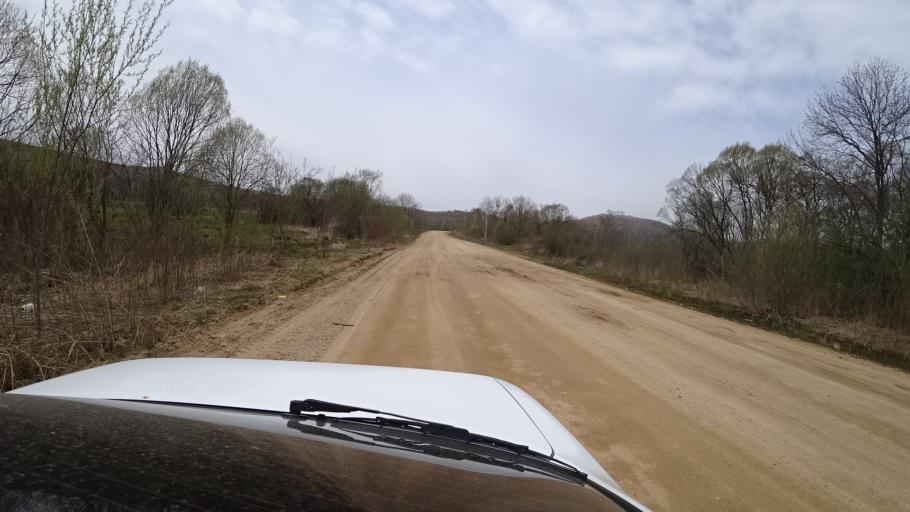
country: RU
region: Primorskiy
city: Dal'nerechensk
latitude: 45.7998
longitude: 134.0979
